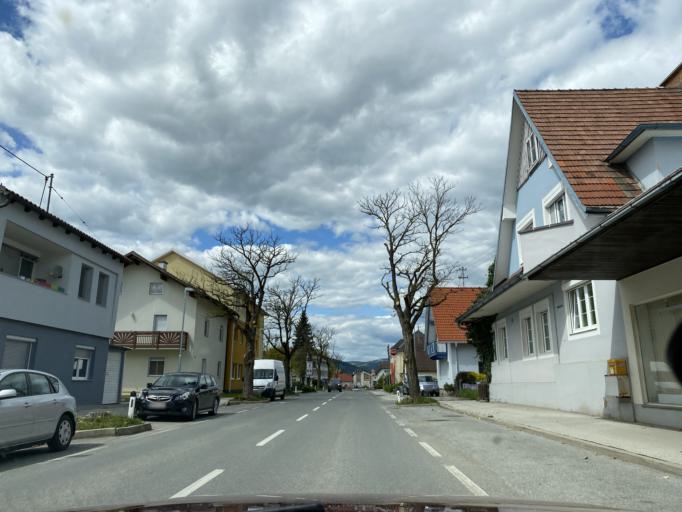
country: AT
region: Carinthia
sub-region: Politischer Bezirk Wolfsberg
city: Wolfsberg
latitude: 46.8033
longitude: 14.8503
